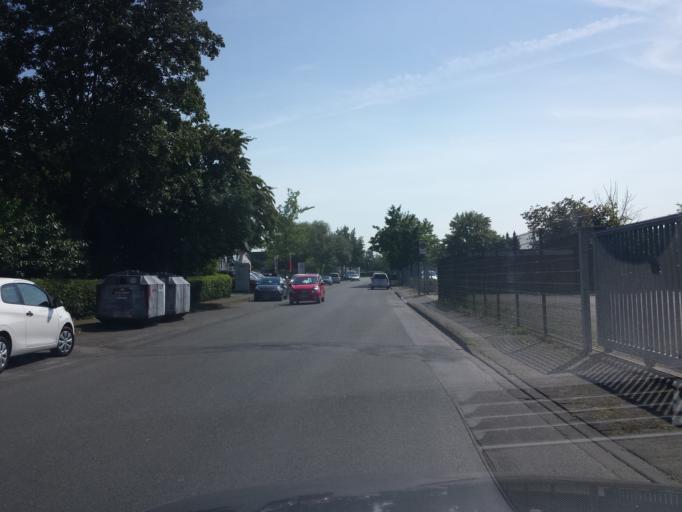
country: DE
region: North Rhine-Westphalia
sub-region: Regierungsbezirk Munster
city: Senden
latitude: 51.8471
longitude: 7.4833
